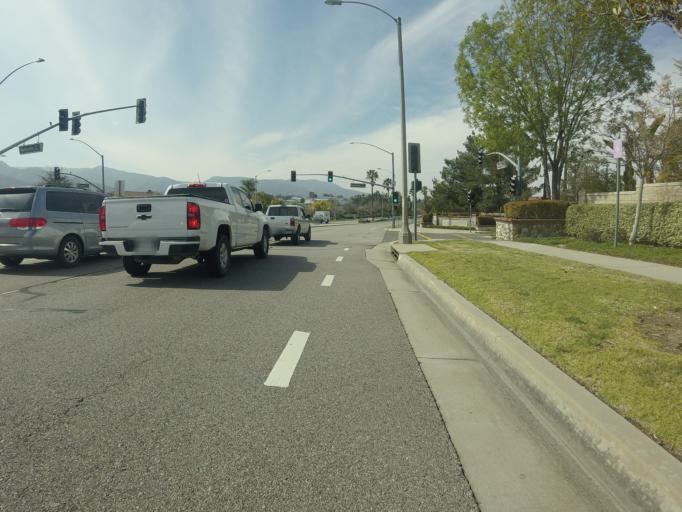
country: US
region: California
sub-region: Riverside County
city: Corona
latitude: 33.8385
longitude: -117.5664
